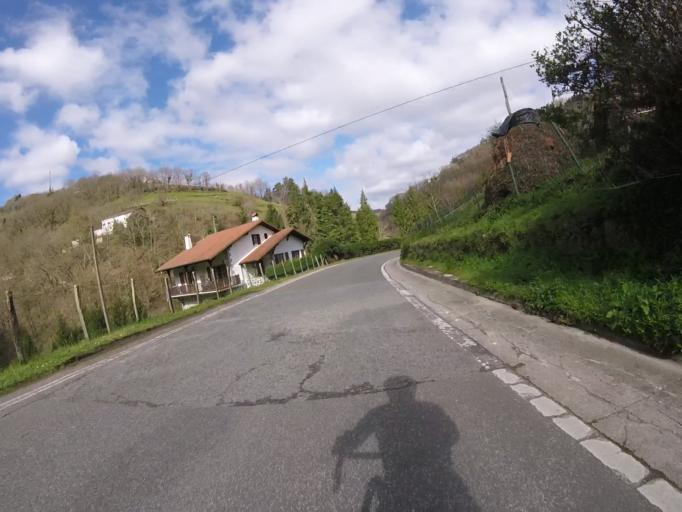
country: ES
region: Navarre
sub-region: Provincia de Navarra
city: Goizueta
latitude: 43.1660
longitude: -1.8583
